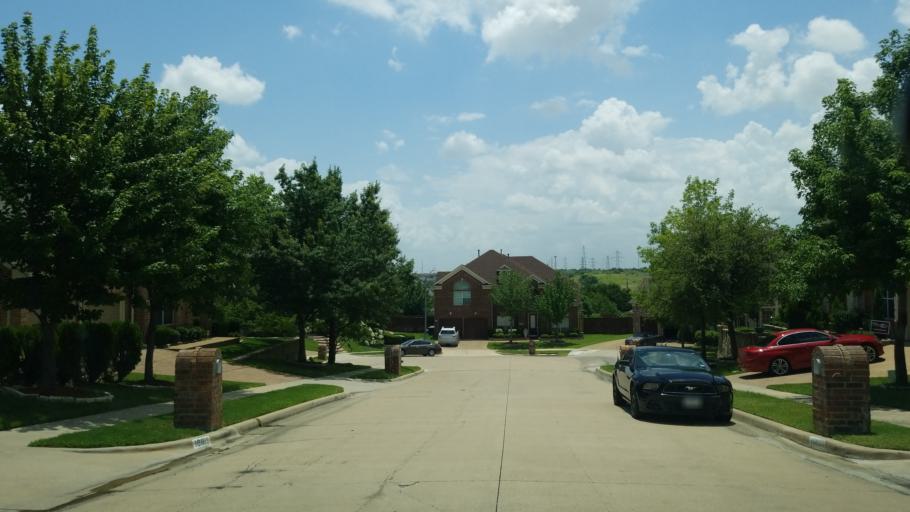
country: US
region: Texas
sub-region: Dallas County
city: Coppell
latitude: 32.9435
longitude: -96.9671
